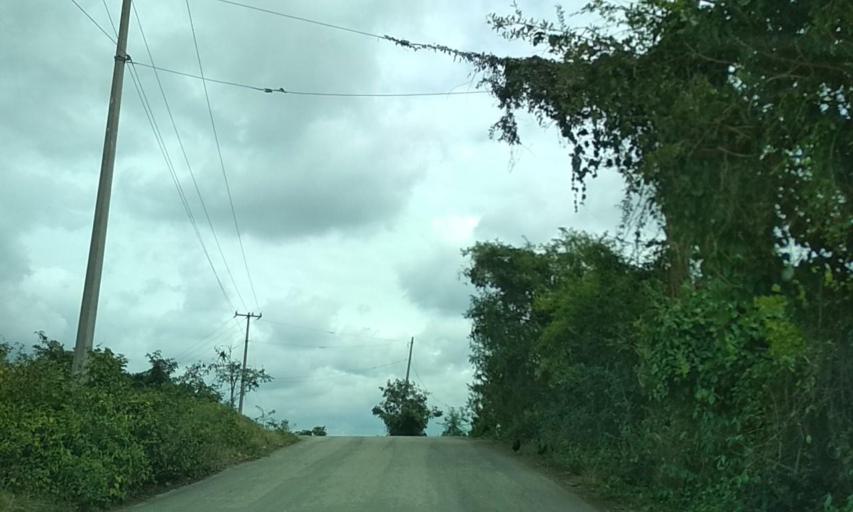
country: MX
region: Veracruz
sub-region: Papantla
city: El Chote
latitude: 20.3553
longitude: -97.3450
